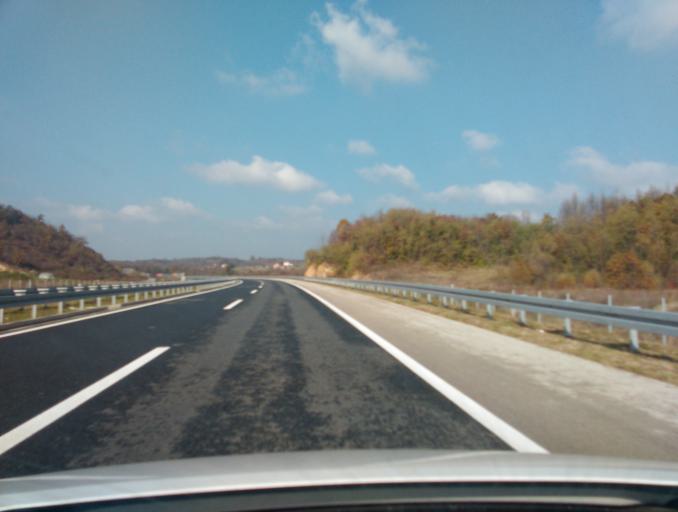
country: BA
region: Republika Srpska
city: Doboj
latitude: 44.8285
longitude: 18.0176
